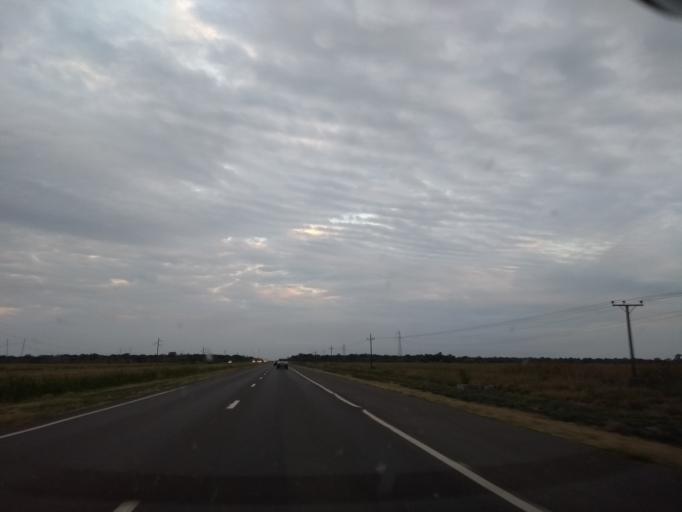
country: AR
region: Chaco
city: Puerto Tirol
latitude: -27.2787
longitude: -59.1354
